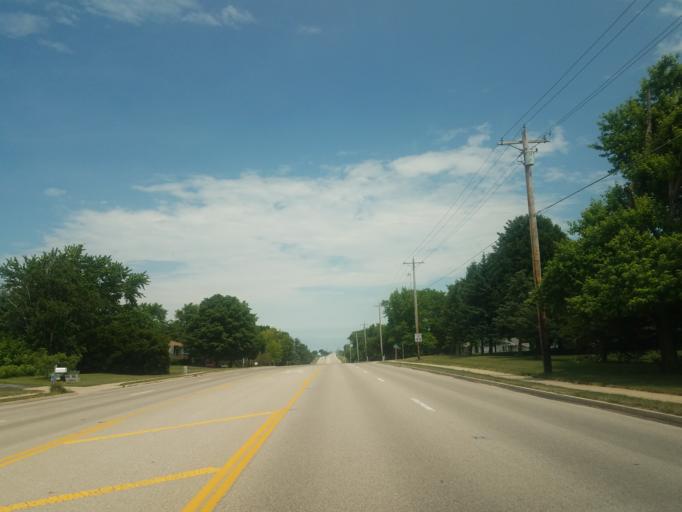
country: US
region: Illinois
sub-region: McLean County
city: Downs
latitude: 40.4221
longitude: -88.9013
